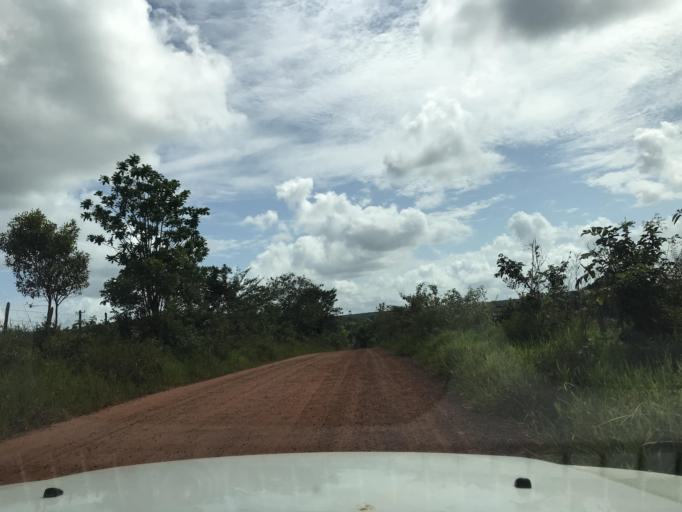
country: BR
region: Bahia
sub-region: Entre Rios
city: Entre Rios
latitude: -12.1694
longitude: -38.0939
